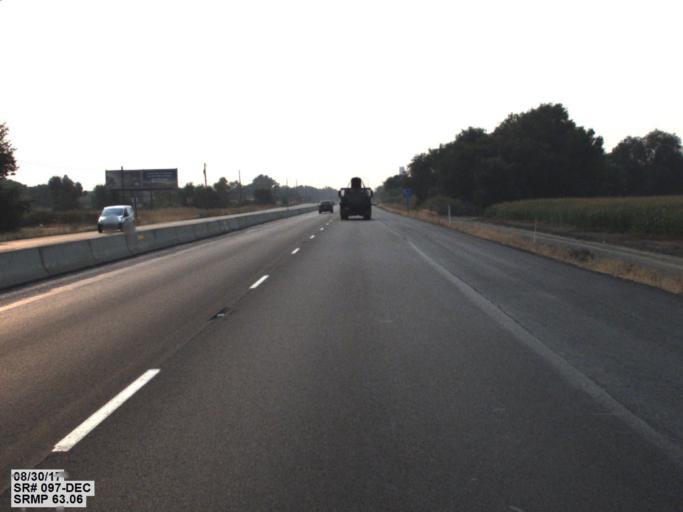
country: US
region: Washington
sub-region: Yakima County
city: Toppenish
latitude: 46.3840
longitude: -120.3473
